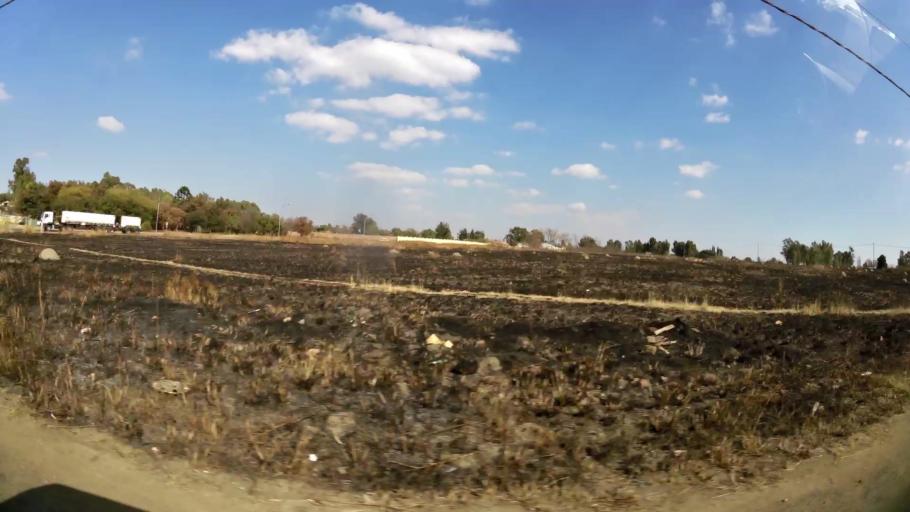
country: ZA
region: Gauteng
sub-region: Ekurhuleni Metropolitan Municipality
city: Benoni
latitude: -26.1014
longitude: 28.3526
